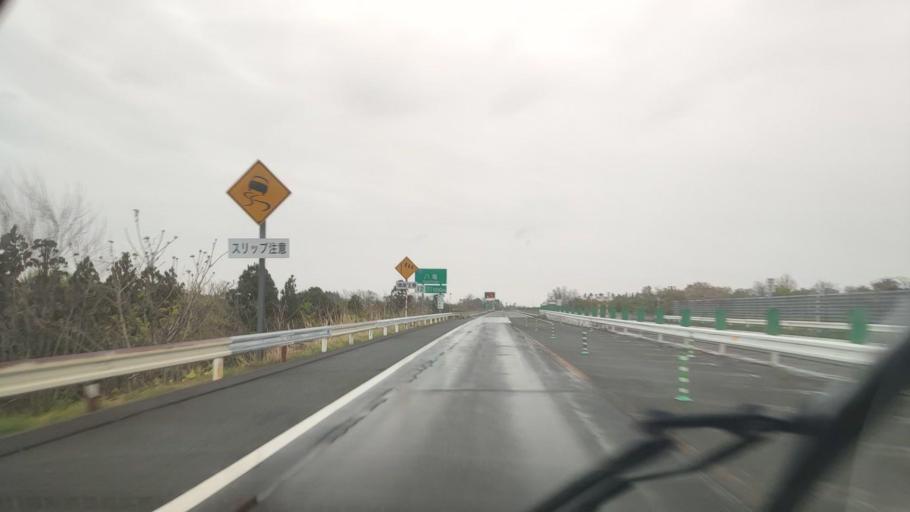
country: JP
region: Akita
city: Noshiromachi
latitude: 40.1266
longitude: 140.0124
